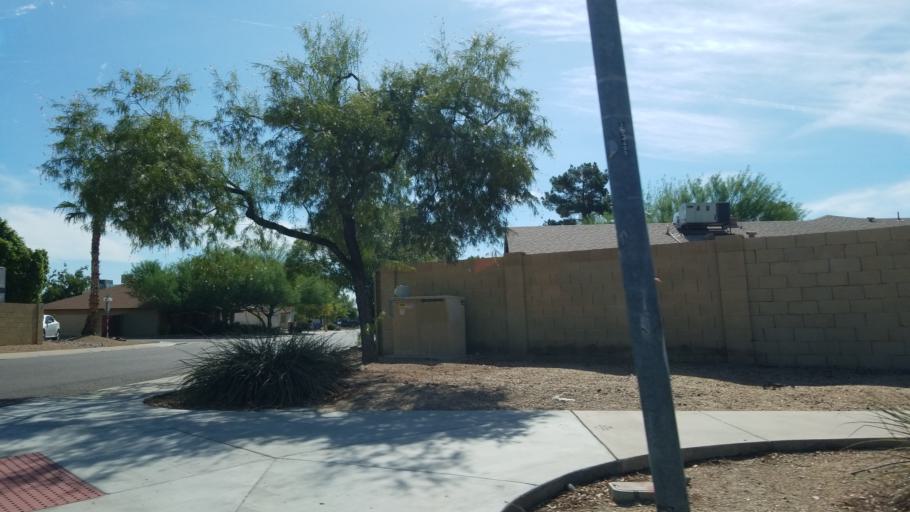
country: US
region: Arizona
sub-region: Maricopa County
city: Peoria
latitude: 33.6430
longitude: -112.1517
